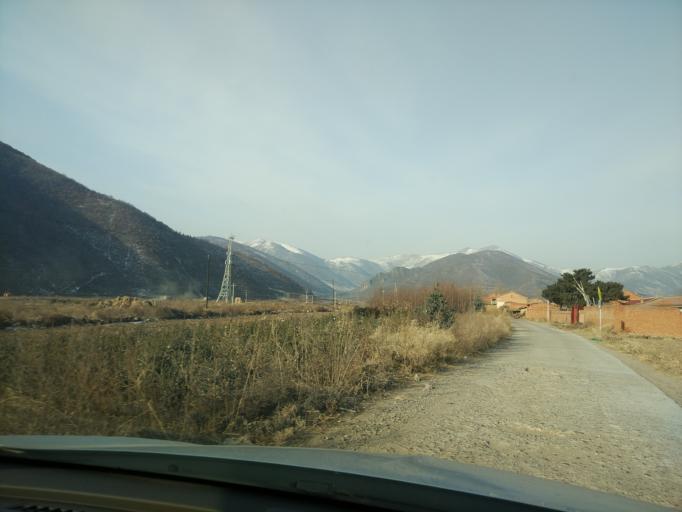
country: CN
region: Hebei
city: Xiwanzi
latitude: 40.8484
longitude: 115.5092
